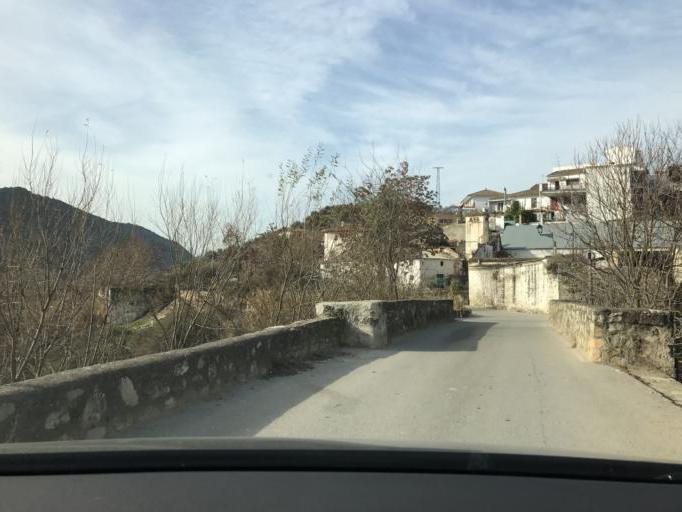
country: ES
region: Andalusia
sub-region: Provincia de Granada
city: Algarinejo
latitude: 37.3233
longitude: -4.1598
